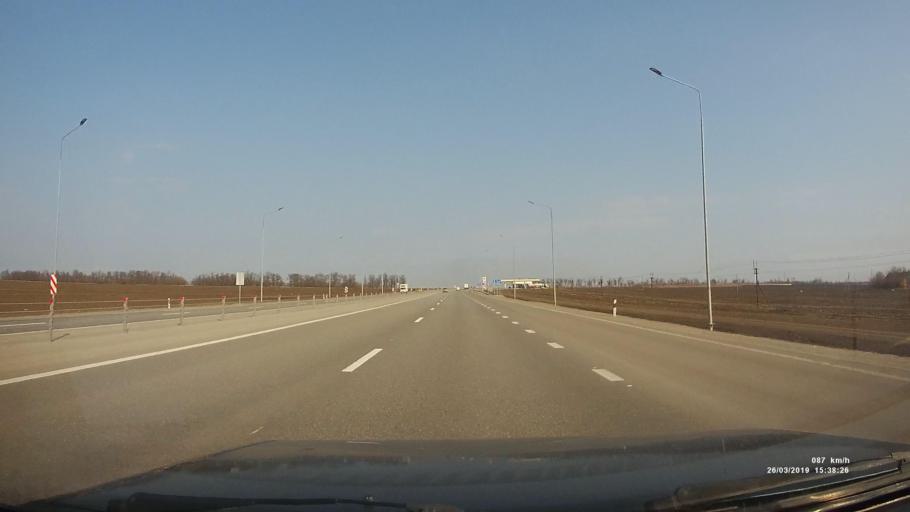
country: RU
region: Rostov
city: Sinyavskoye
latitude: 47.2950
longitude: 39.2687
